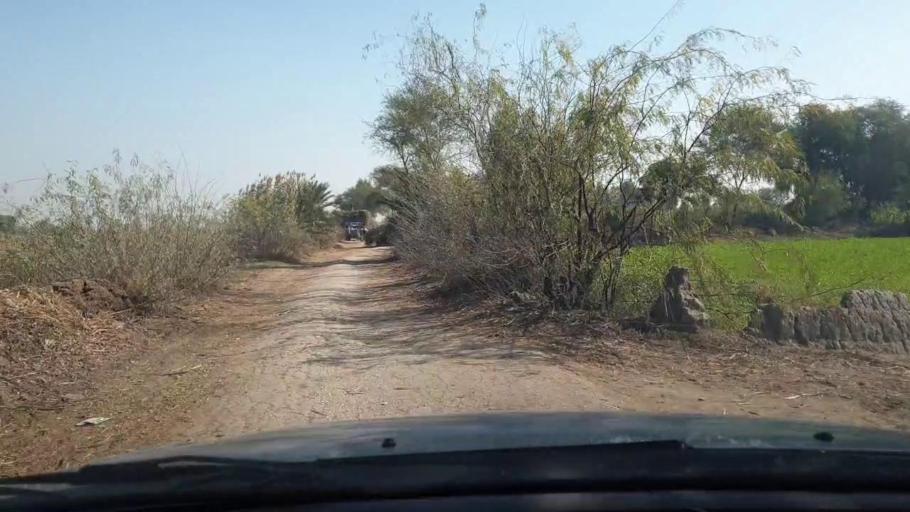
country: PK
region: Sindh
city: Mirpur Mathelo
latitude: 28.0668
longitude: 69.5038
